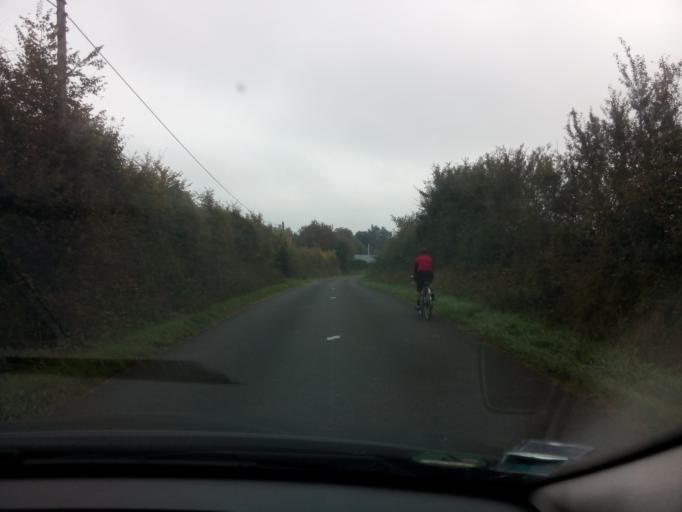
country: FR
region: Pays de la Loire
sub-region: Departement de Maine-et-Loire
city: Soulaire-et-Bourg
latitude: 47.5930
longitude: -0.5522
